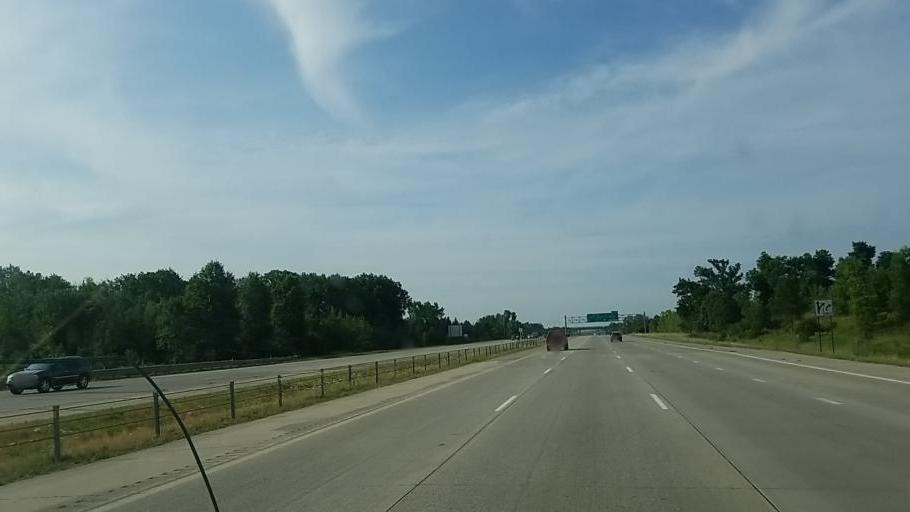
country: US
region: Michigan
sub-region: Eaton County
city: Waverly
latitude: 42.7319
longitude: -84.6687
